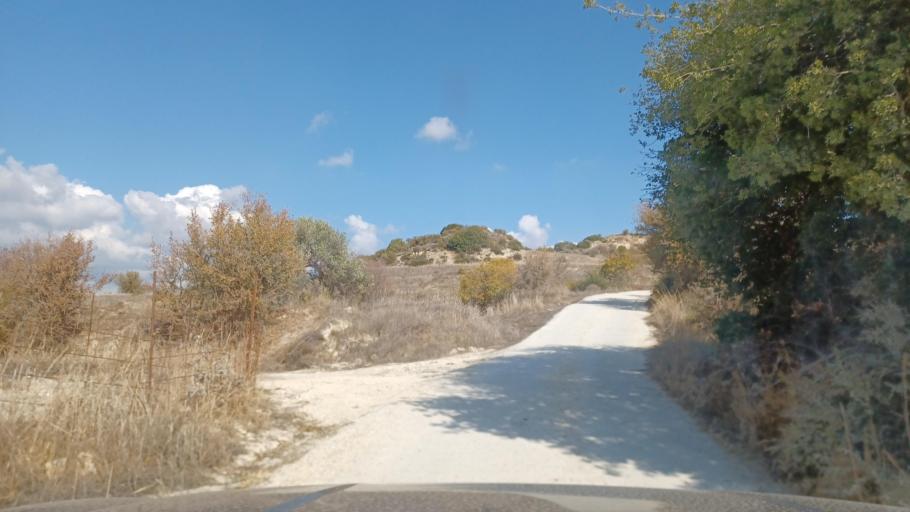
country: CY
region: Pafos
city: Mesogi
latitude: 34.8417
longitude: 32.5706
